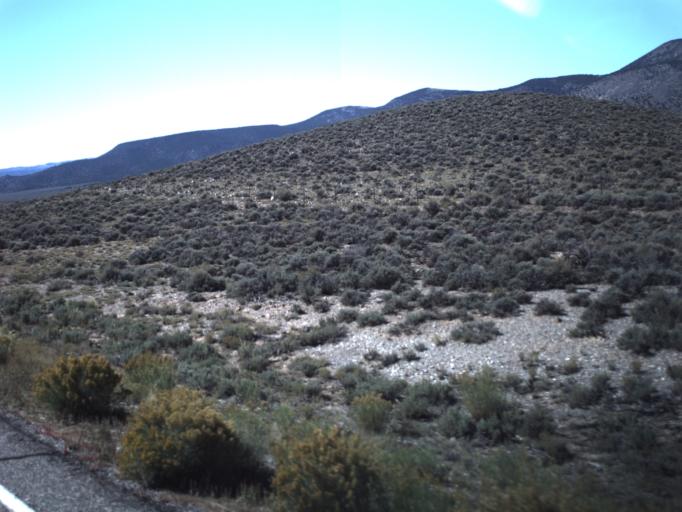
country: US
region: Utah
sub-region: Piute County
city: Junction
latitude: 38.2363
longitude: -111.9892
